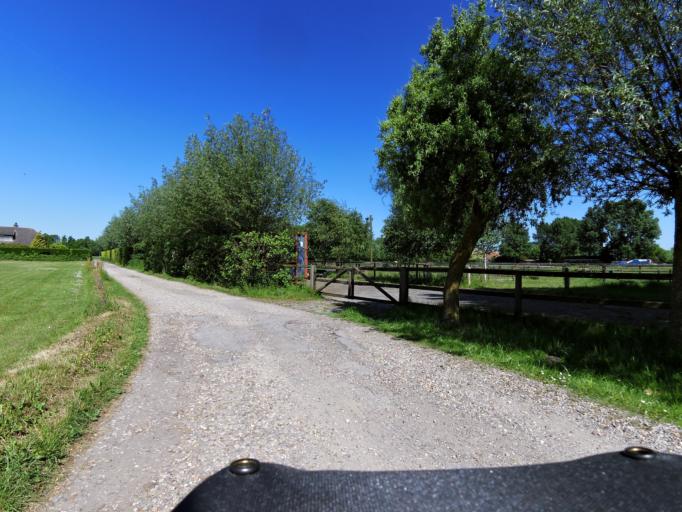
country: NL
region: South Holland
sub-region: Gemeente Hellevoetsluis
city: Nieuw-Helvoet
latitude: 51.8905
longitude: 4.0821
